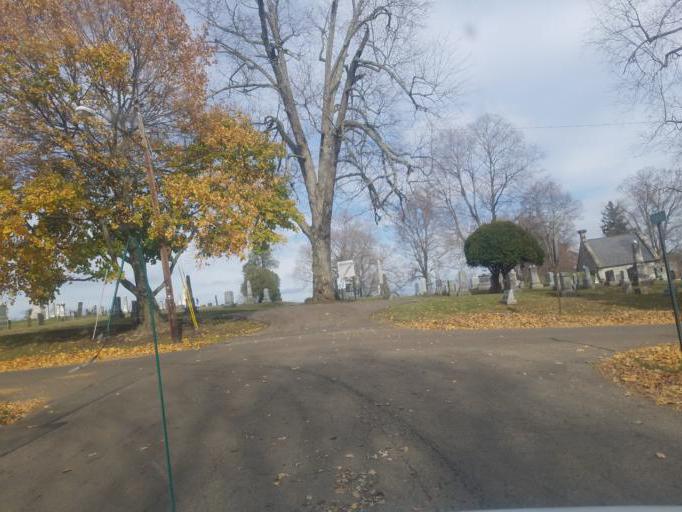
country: US
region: Ohio
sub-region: Knox County
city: Mount Vernon
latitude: 40.4026
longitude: -82.4839
